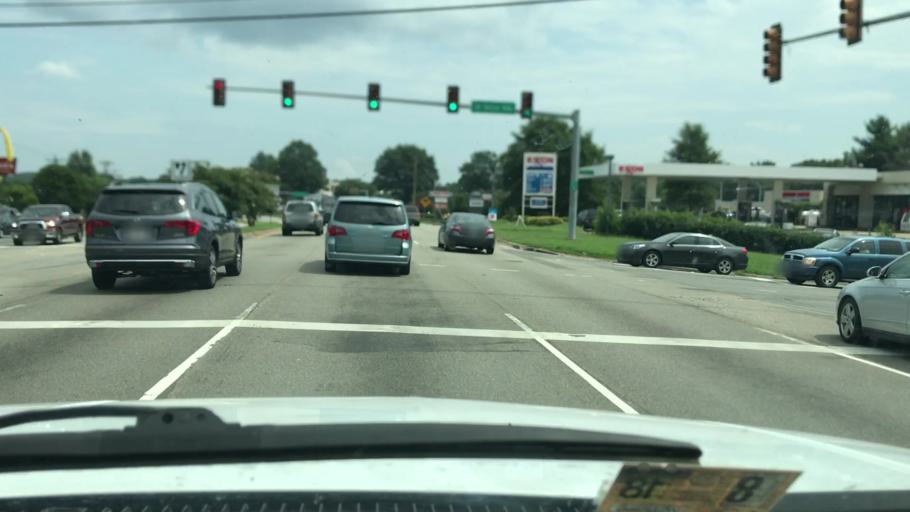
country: US
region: Virginia
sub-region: Chesterfield County
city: Bon Air
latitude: 37.4985
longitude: -77.5692
